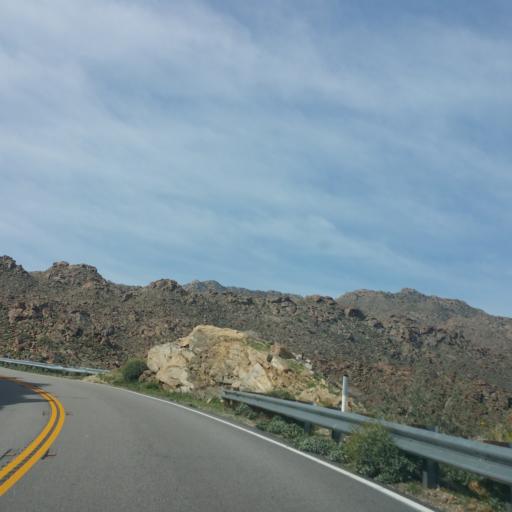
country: US
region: California
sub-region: Riverside County
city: Palm Desert
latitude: 33.6499
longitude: -116.4048
